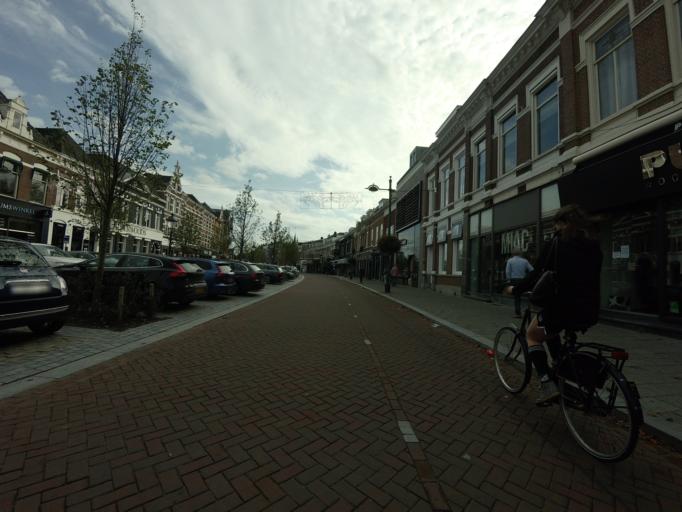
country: NL
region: North Brabant
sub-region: Gemeente Breda
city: Breda
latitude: 51.5801
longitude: 4.7776
